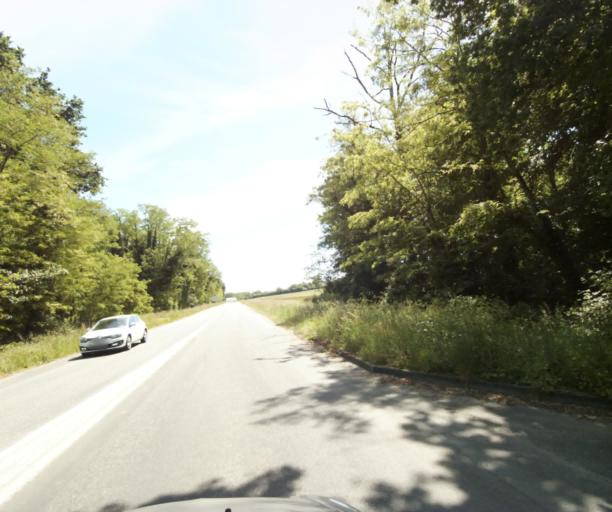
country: FR
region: Centre
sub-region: Departement d'Indre-et-Loire
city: Ligre
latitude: 47.1358
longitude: 0.2933
